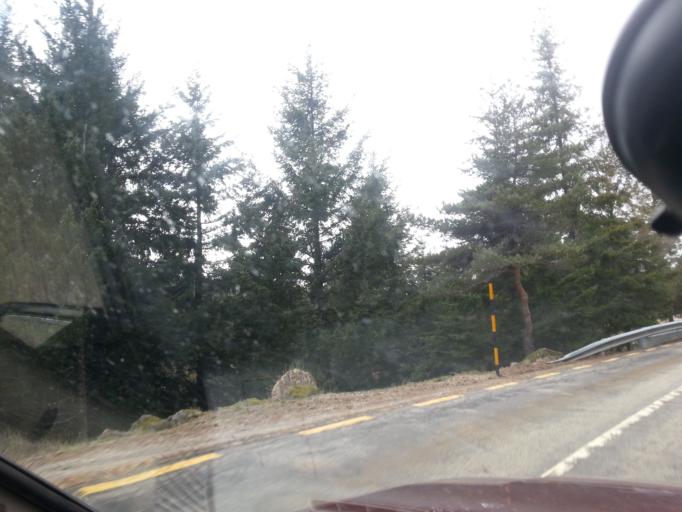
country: PT
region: Guarda
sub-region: Manteigas
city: Manteigas
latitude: 40.4123
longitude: -7.5638
